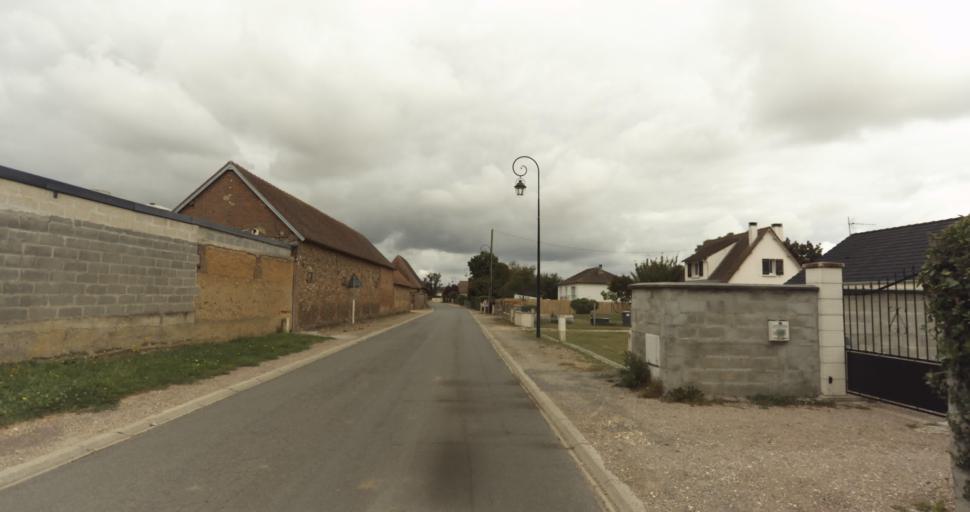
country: FR
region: Haute-Normandie
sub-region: Departement de l'Eure
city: Gravigny
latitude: 48.9871
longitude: 1.2542
